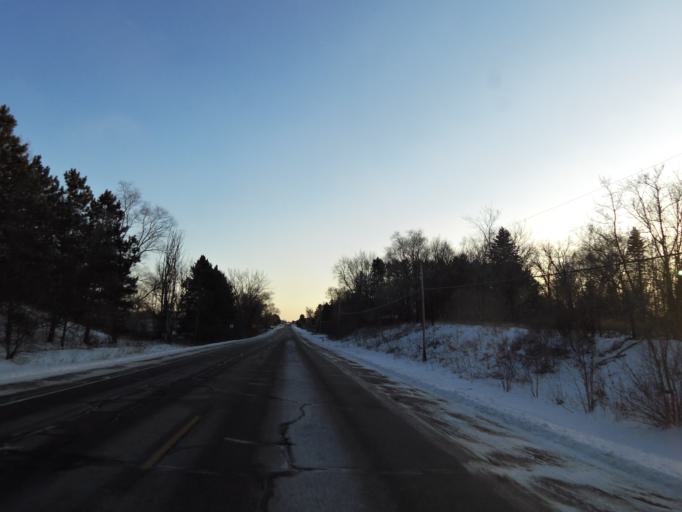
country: US
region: Minnesota
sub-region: Washington County
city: Lake Elmo
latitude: 44.9716
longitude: -92.8831
